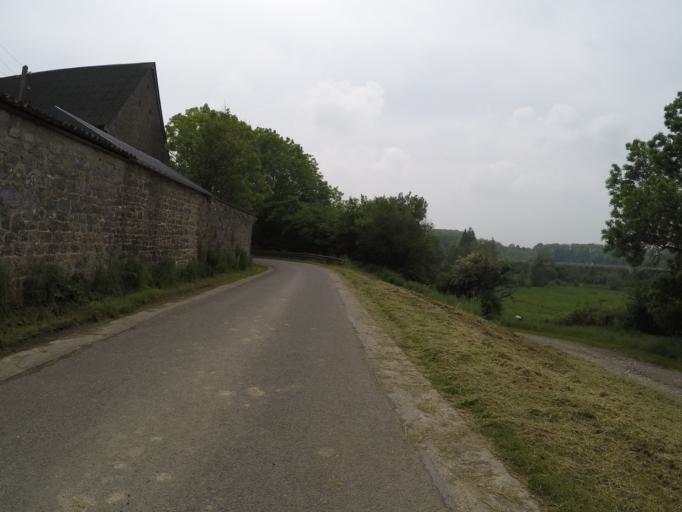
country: BE
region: Wallonia
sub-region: Province de Namur
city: Ciney
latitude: 50.3256
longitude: 5.0680
